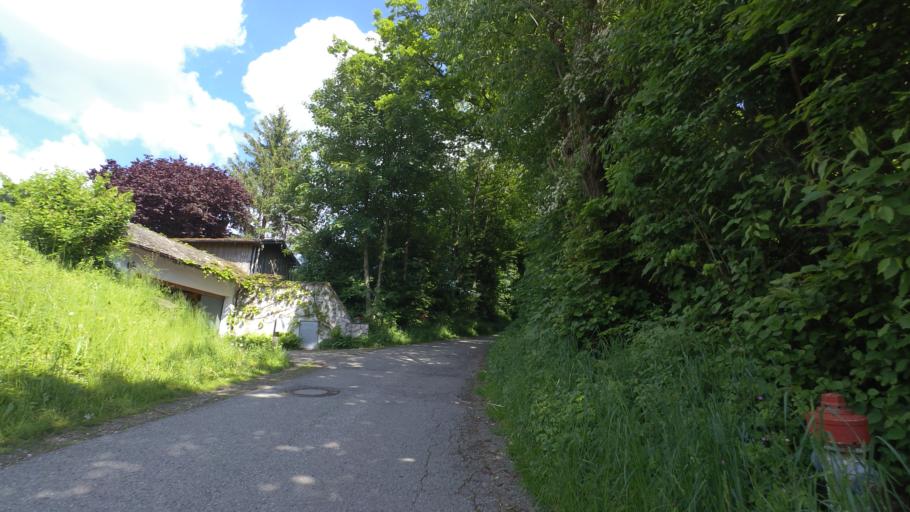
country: DE
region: Bavaria
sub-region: Upper Bavaria
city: Vachendorf
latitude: 47.8735
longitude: 12.5972
